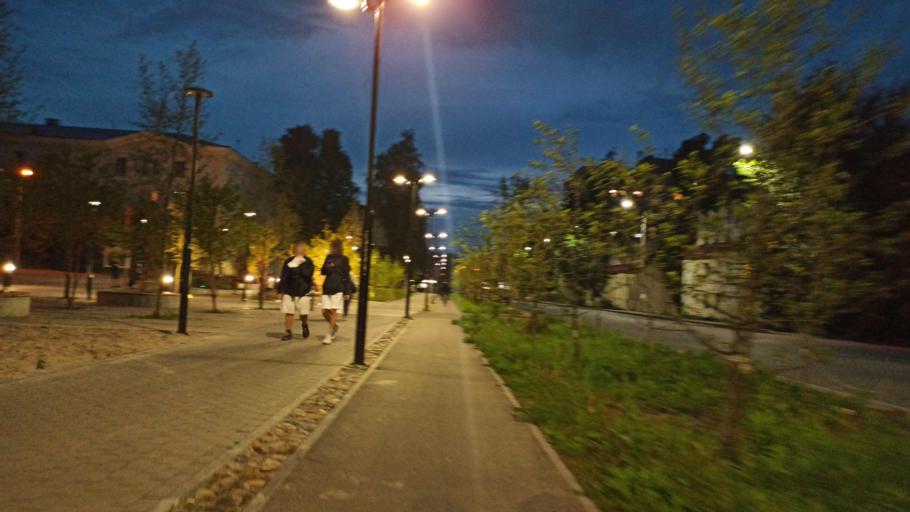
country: RU
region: Tomsk
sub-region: Tomskiy Rayon
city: Tomsk
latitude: 56.4639
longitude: 84.9607
